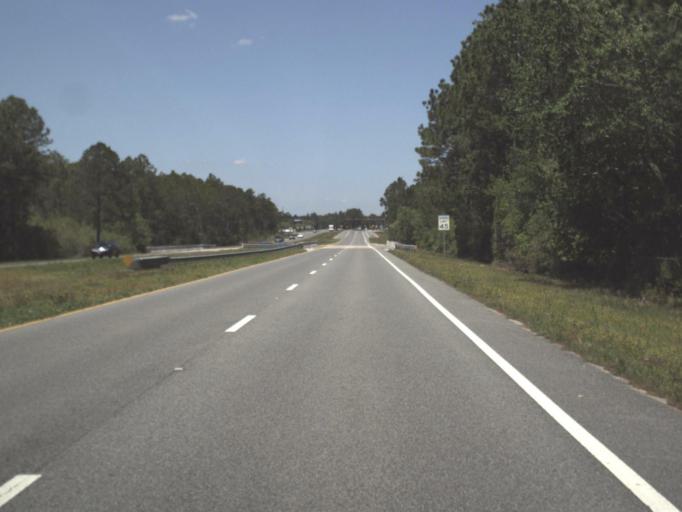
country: US
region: Florida
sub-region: Escambia County
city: Myrtle Grove
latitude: 30.3563
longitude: -87.3564
